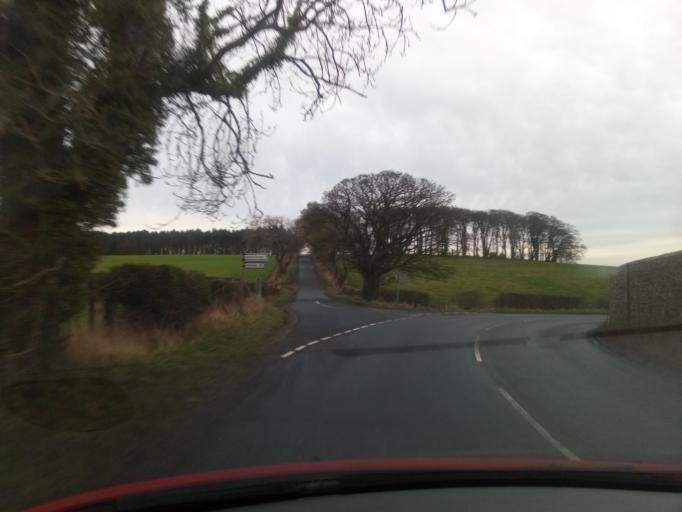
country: GB
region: England
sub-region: Northumberland
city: Alnwick
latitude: 55.4434
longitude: -1.7324
